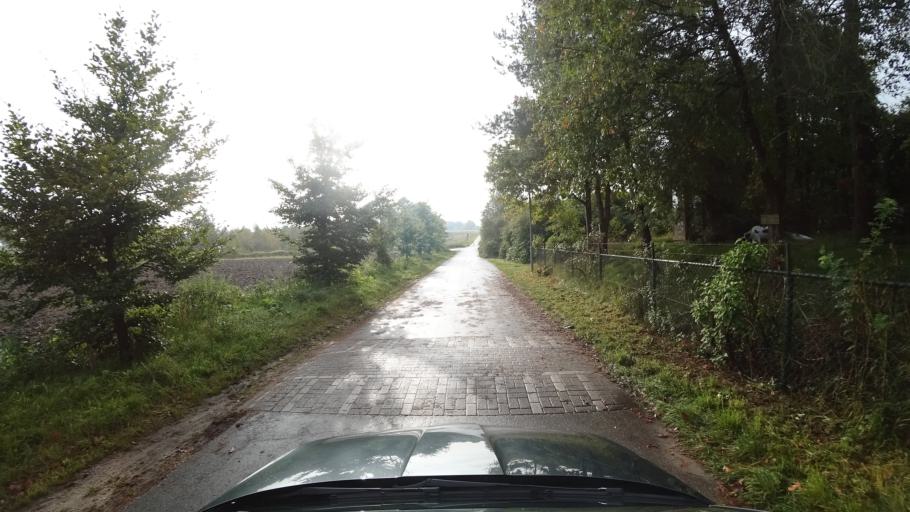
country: NL
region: Gelderland
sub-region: Gemeente Renkum
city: Renkum
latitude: 51.9911
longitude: 5.7408
